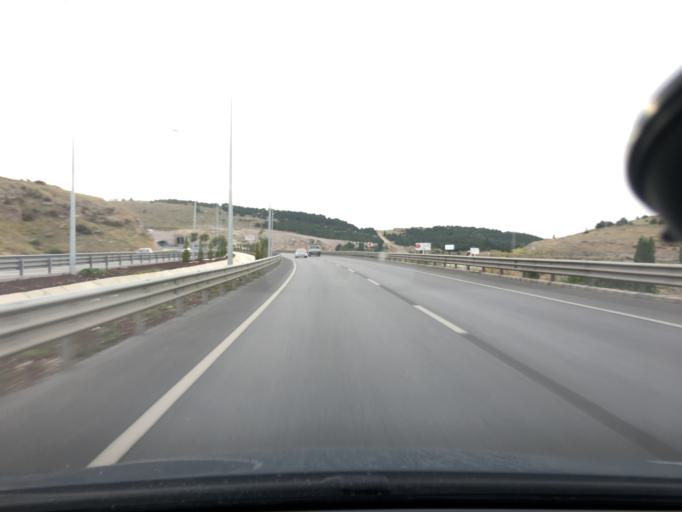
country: TR
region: Afyonkarahisar
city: Afyonkarahisar
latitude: 38.7948
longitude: 30.4423
